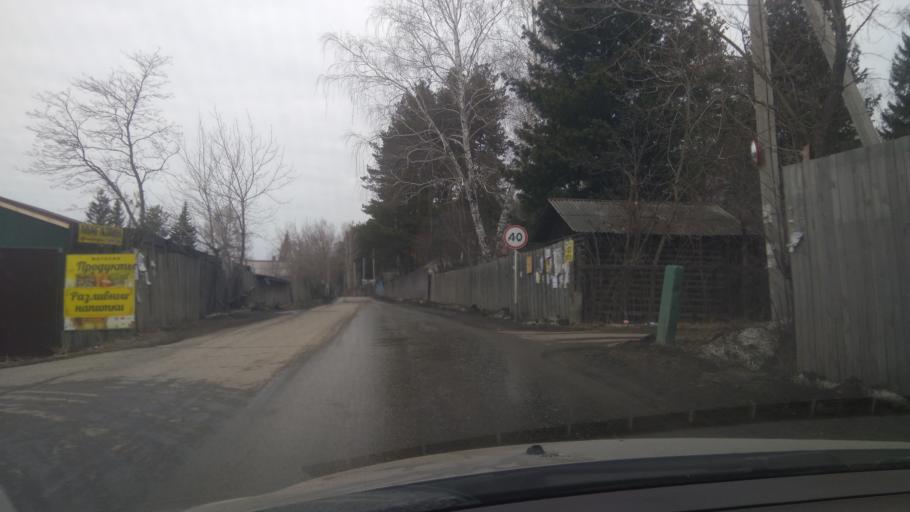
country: RU
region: Sverdlovsk
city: Severka
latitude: 56.8490
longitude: 60.3841
